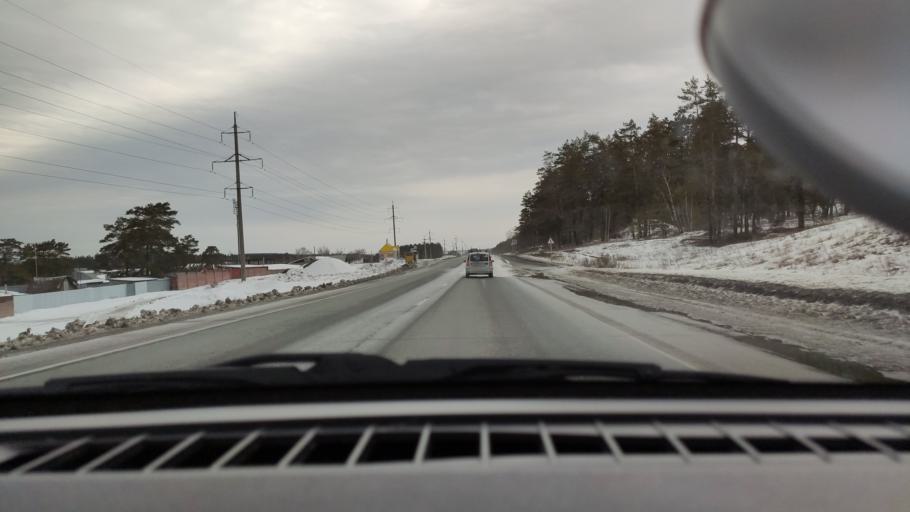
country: RU
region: Samara
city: Volzhskiy
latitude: 53.4600
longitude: 50.0811
